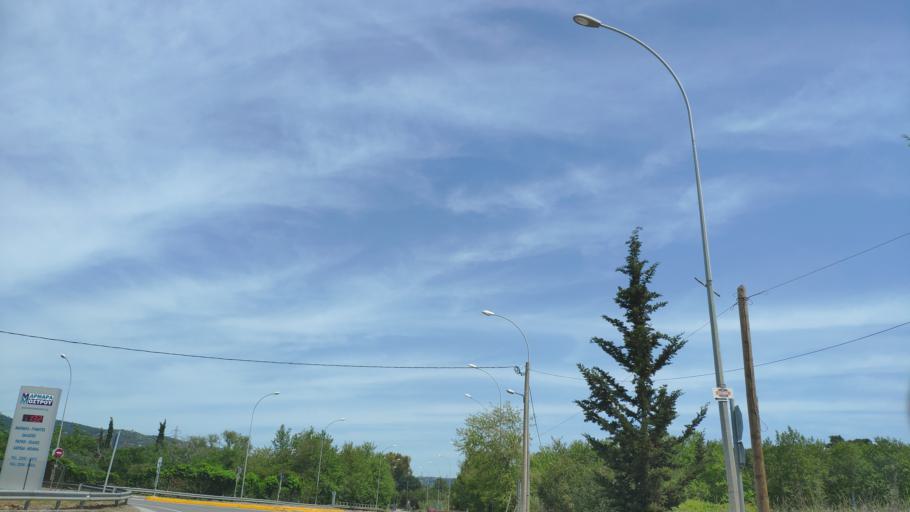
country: GR
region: Attica
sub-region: Nomarchia Anatolikis Attikis
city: Afidnes
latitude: 38.1878
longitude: 23.8545
